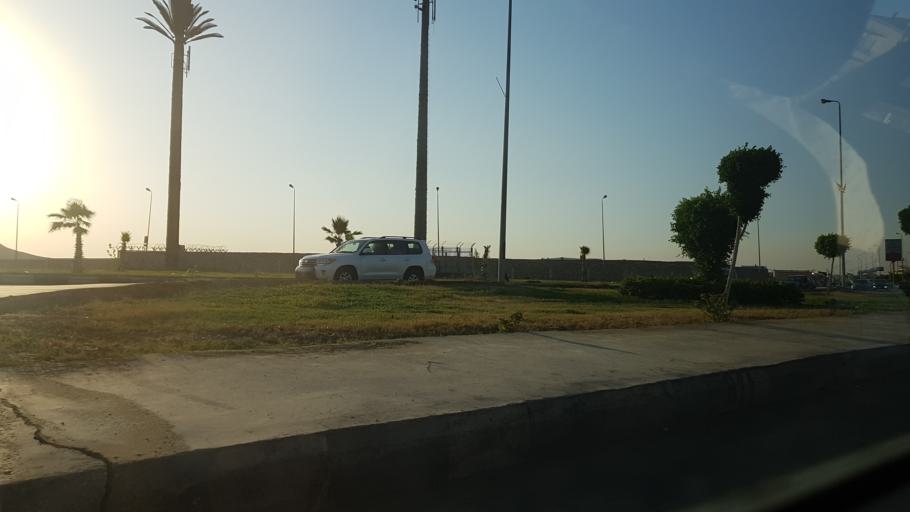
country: EG
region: Muhafazat al Qalyubiyah
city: Al Khankah
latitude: 30.0462
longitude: 31.4424
